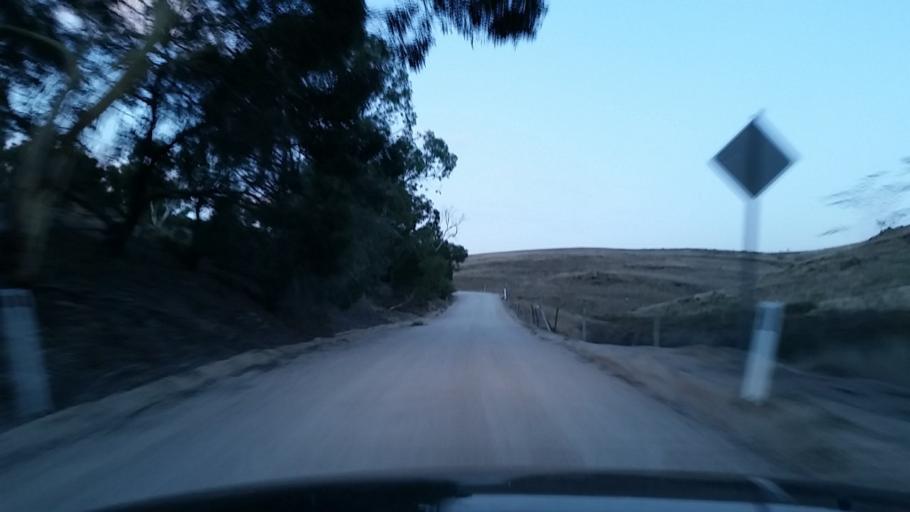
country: AU
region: South Australia
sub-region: Mount Barker
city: Callington
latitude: -35.1003
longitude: 138.9872
